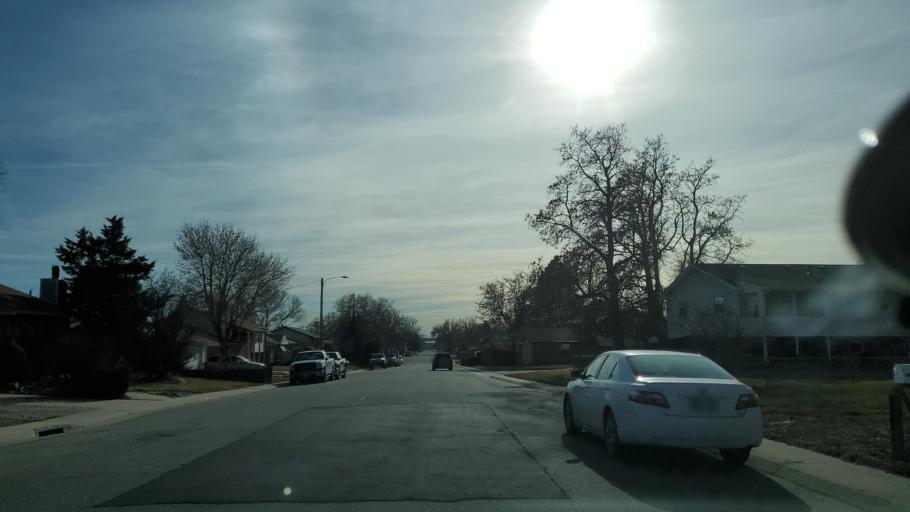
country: US
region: Colorado
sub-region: Adams County
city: Northglenn
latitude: 39.9069
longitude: -104.9604
